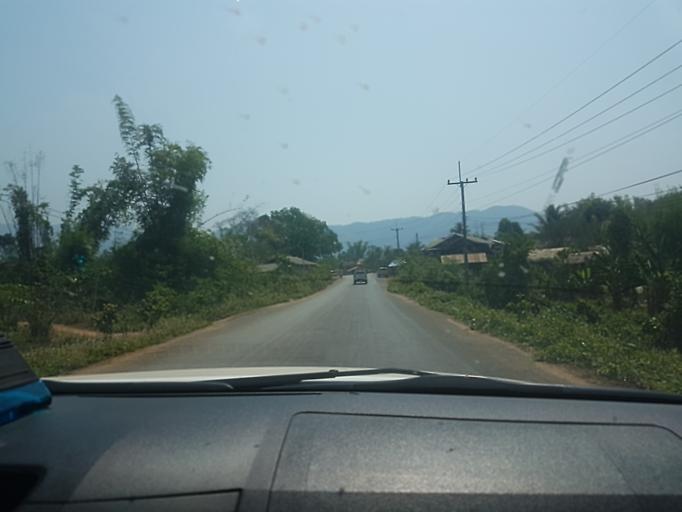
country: LA
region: Bolikhamxai
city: Ban Nahin
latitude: 18.5334
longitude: 104.4798
